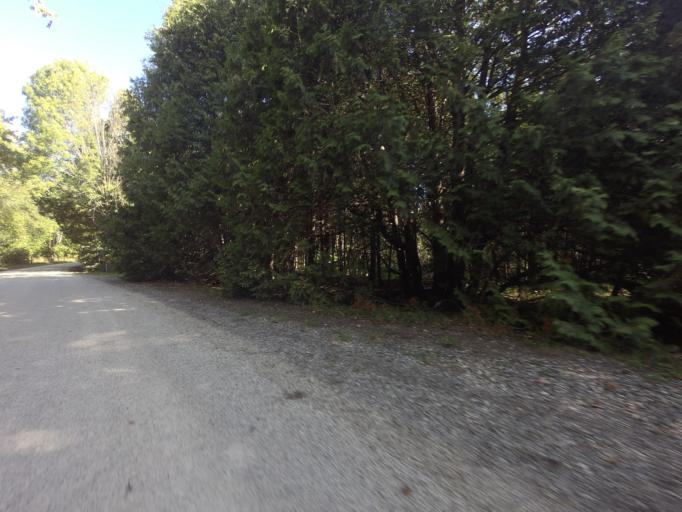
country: CA
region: Ontario
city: Waterloo
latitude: 43.6637
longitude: -80.4529
